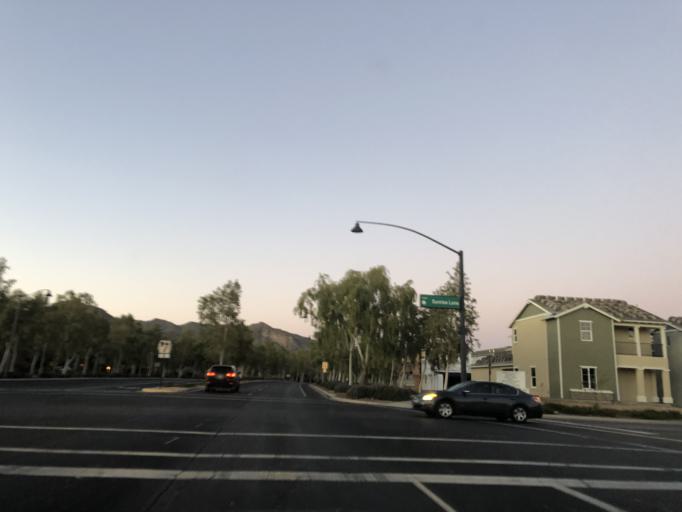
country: US
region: Arizona
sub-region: Maricopa County
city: Citrus Park
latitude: 33.4976
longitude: -112.5134
